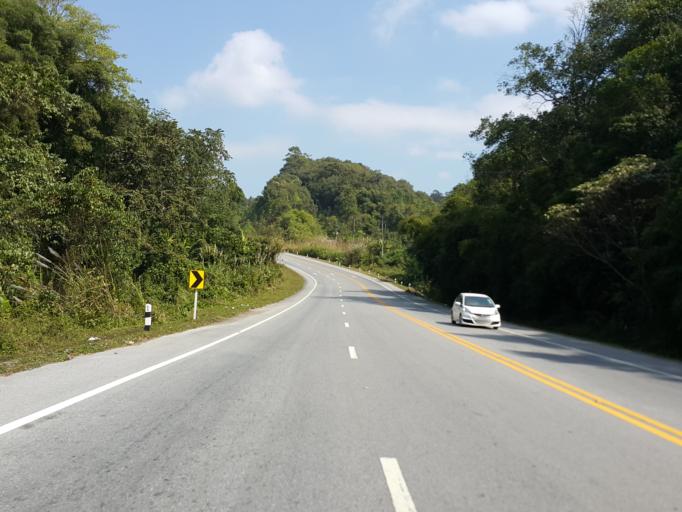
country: TH
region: Lampang
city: Wang Nuea
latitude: 19.0648
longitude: 99.3729
